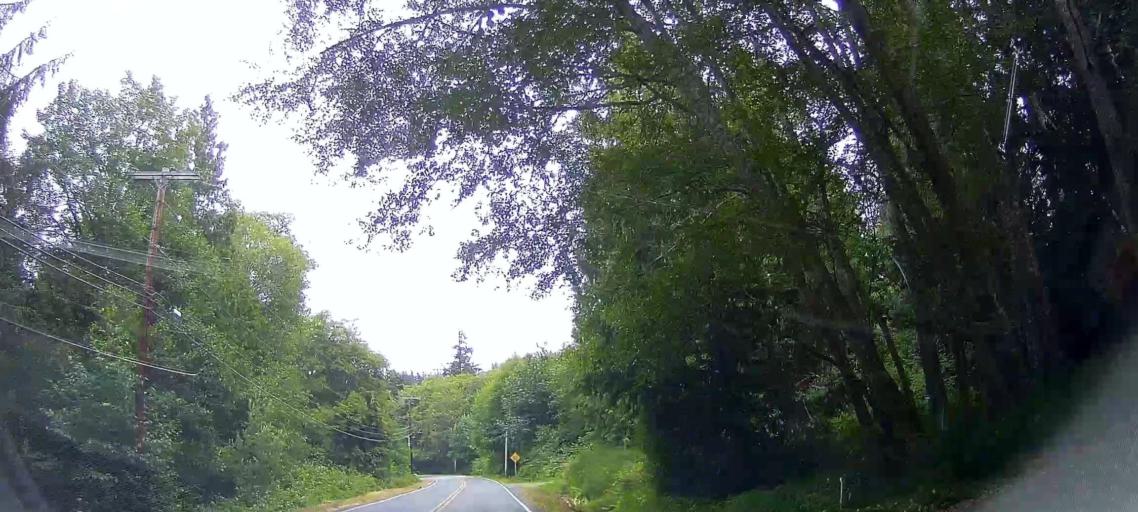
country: US
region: Washington
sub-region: Skagit County
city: Anacortes
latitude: 48.4496
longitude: -122.6433
